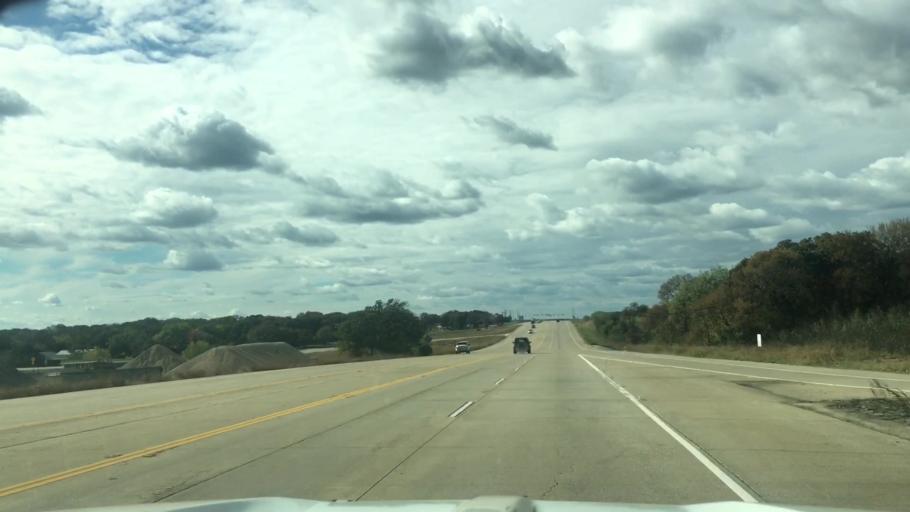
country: US
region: Texas
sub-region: Denton County
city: Cross Roads
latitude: 33.2322
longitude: -97.0069
